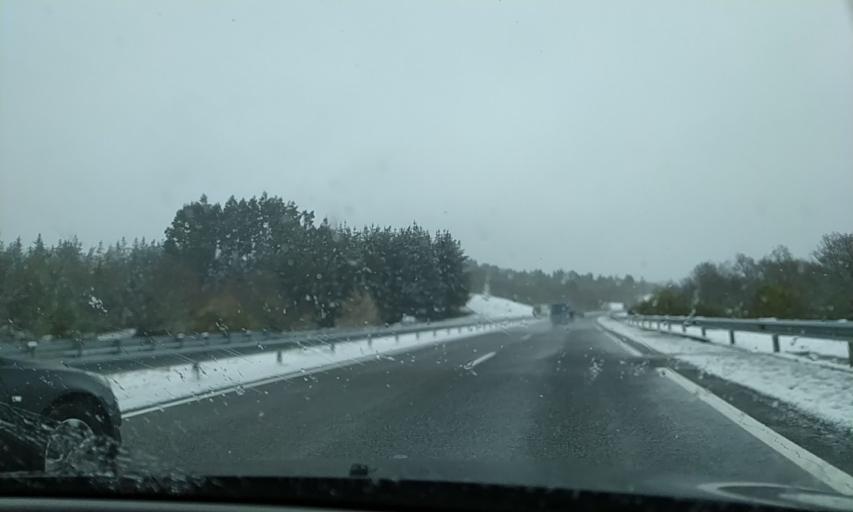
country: ES
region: Galicia
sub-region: Provincia de Ourense
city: Rios
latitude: 41.9784
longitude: -7.3135
